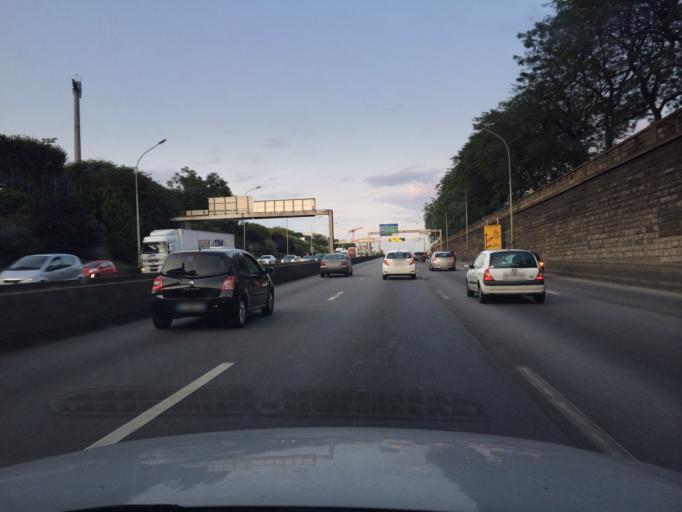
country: FR
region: Ile-de-France
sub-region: Departement du Val-de-Marne
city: Le Kremlin-Bicetre
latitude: 48.8175
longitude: 2.3671
